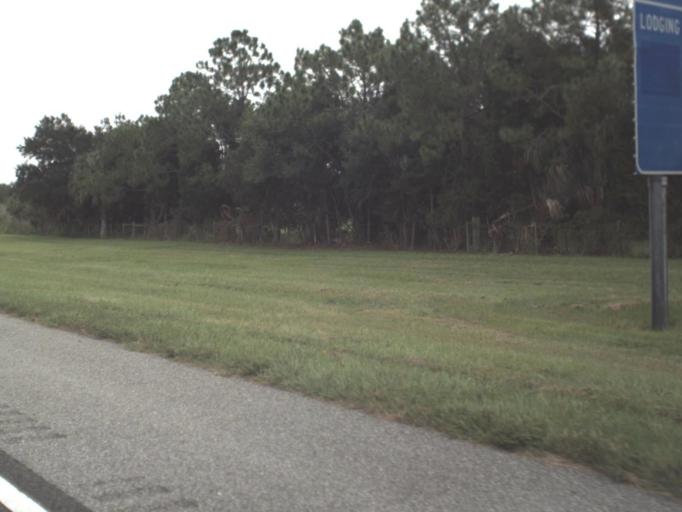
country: US
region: Florida
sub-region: Manatee County
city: Memphis
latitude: 27.5846
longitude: -82.5554
